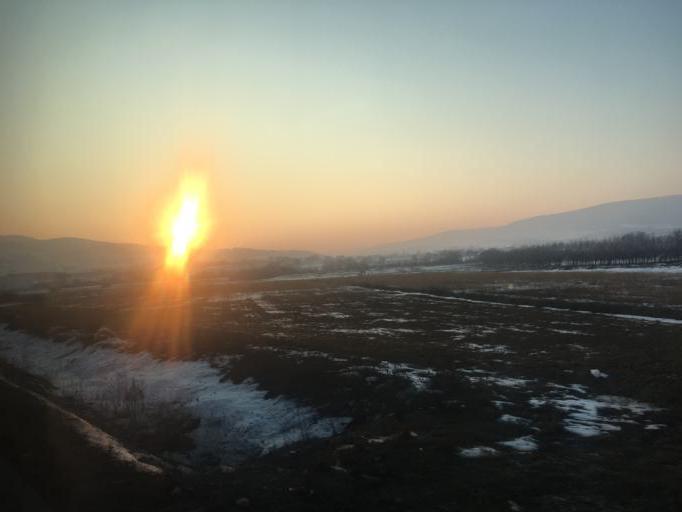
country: XK
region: Pristina
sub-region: Komuna e Drenasit
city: Glogovac
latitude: 42.5829
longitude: 20.8969
